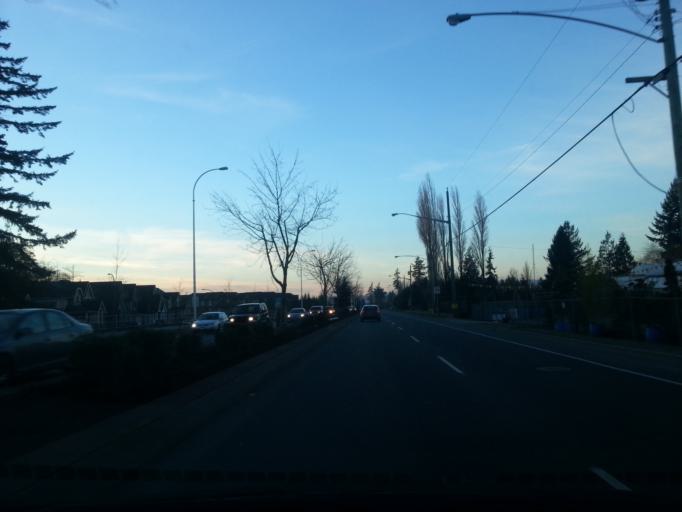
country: CA
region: British Columbia
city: Langley
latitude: 49.1294
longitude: -122.7142
